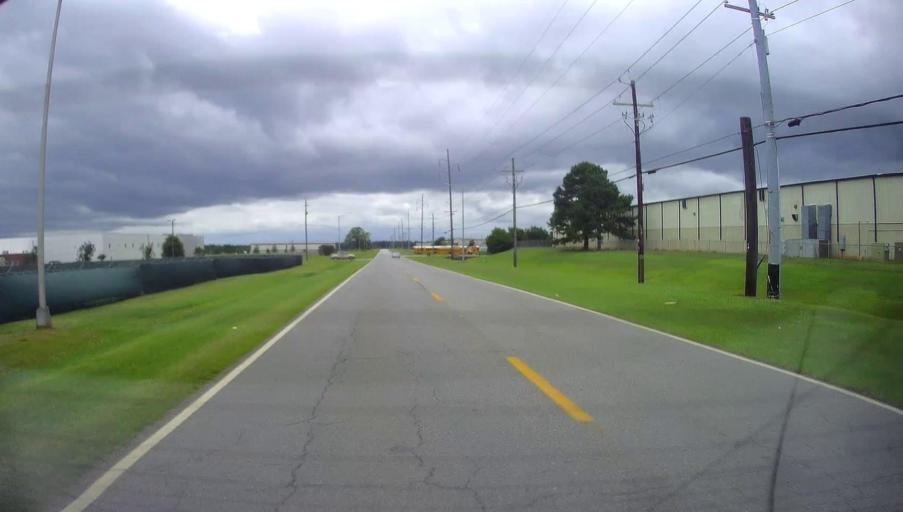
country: US
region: Georgia
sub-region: Bibb County
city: Macon
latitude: 32.8060
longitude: -83.5503
